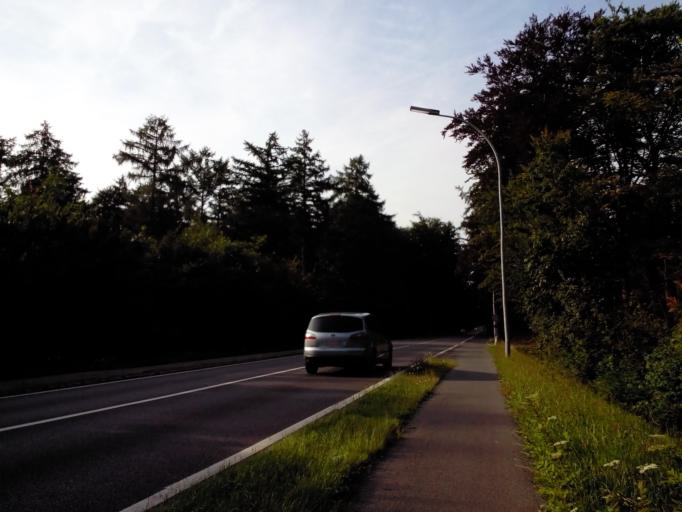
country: BE
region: Flanders
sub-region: Provincie Vlaams-Brabant
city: Oud-Heverlee
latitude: 50.8377
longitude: 4.6984
